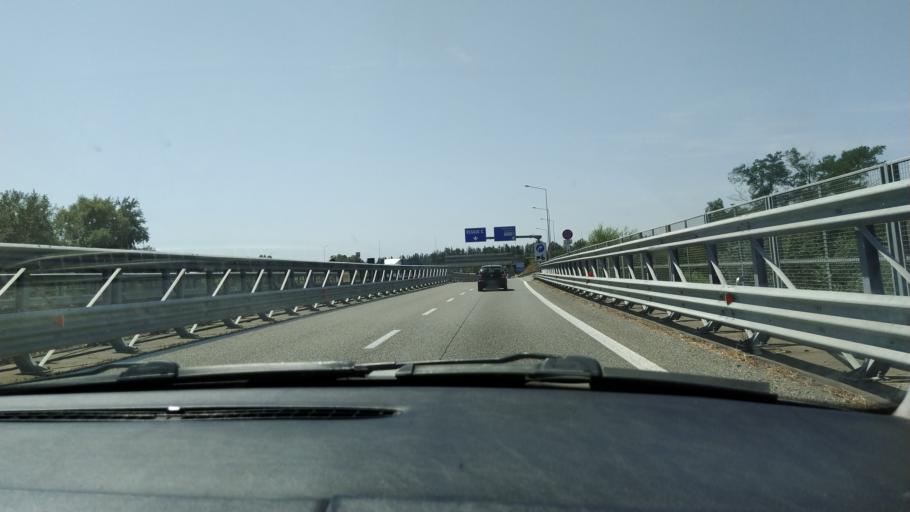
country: IT
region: Basilicate
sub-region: Provincia di Matera
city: Marconia
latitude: 40.3669
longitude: 16.7817
